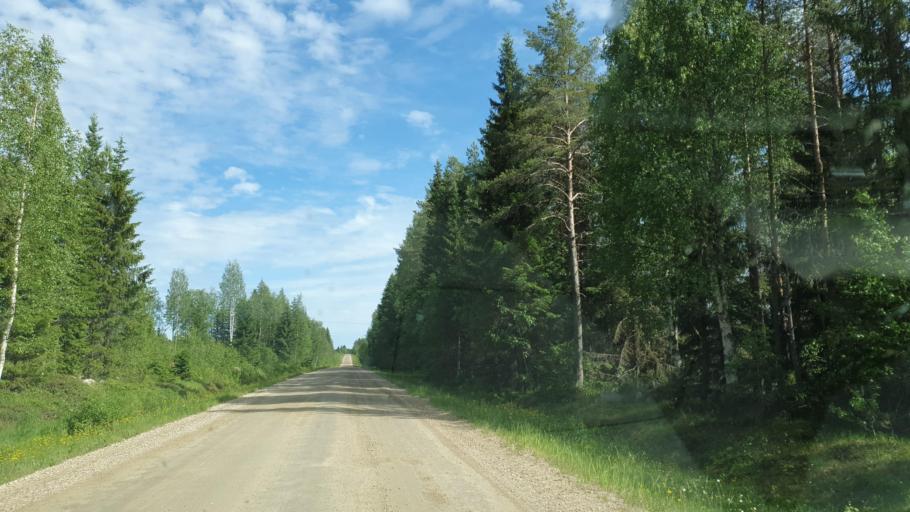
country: FI
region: Kainuu
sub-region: Kehys-Kainuu
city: Kuhmo
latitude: 64.5134
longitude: 29.4512
